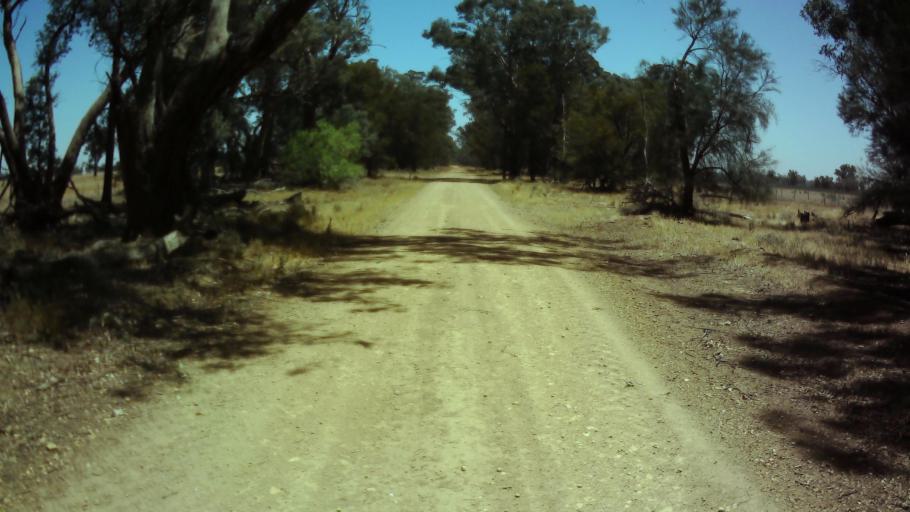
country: AU
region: New South Wales
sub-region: Weddin
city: Grenfell
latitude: -34.0362
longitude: 147.8569
